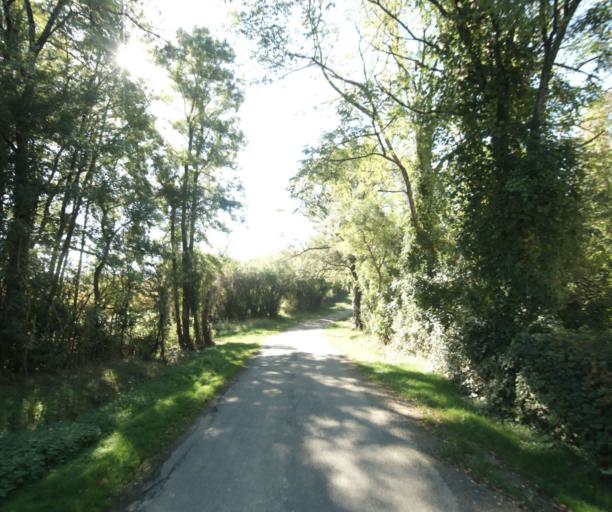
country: FR
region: Midi-Pyrenees
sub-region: Departement du Gers
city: Eauze
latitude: 43.8156
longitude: 0.1620
